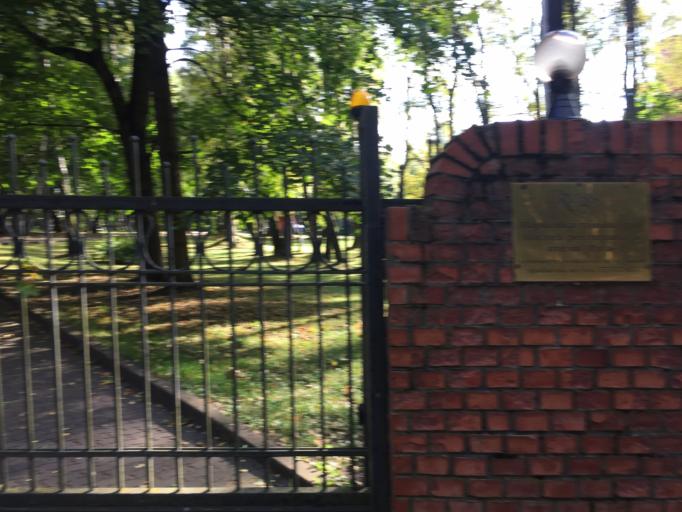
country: RU
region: Kaliningrad
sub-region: Gorod Svetlogorsk
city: Svetlogorsk
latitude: 54.9470
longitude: 20.1652
